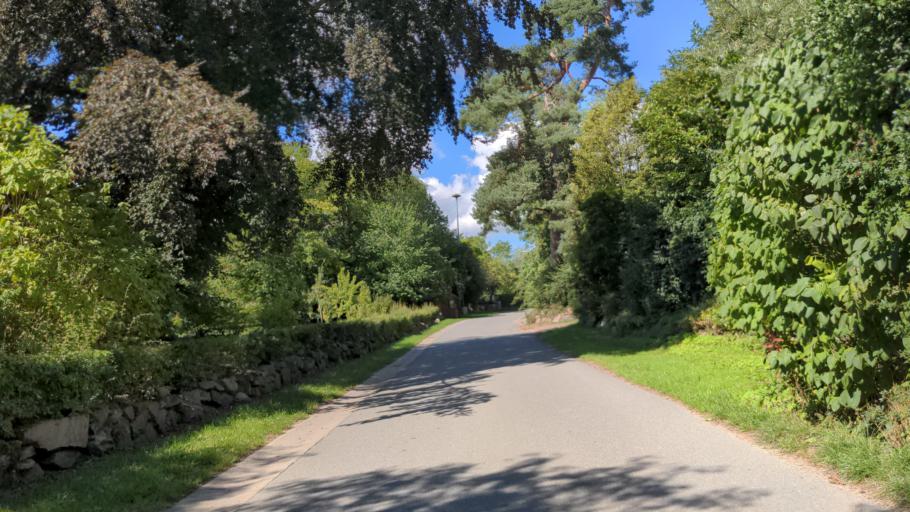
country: DE
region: Schleswig-Holstein
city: Beschendorf
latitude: 54.1777
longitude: 10.8422
